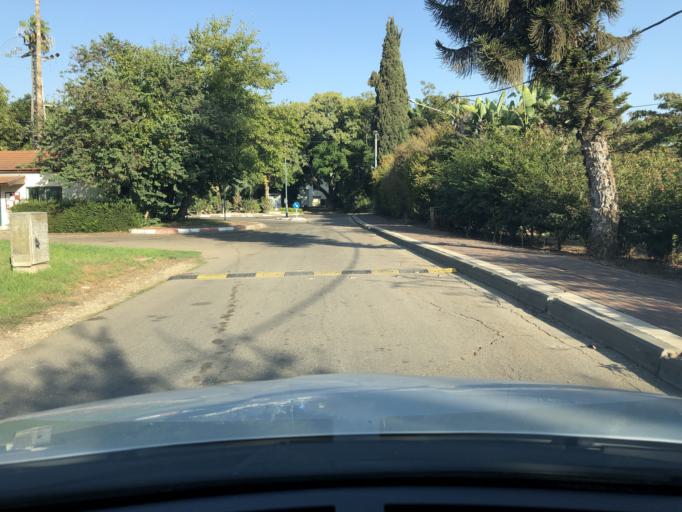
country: IL
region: Central District
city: Hod HaSharon
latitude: 32.1391
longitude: 34.9072
